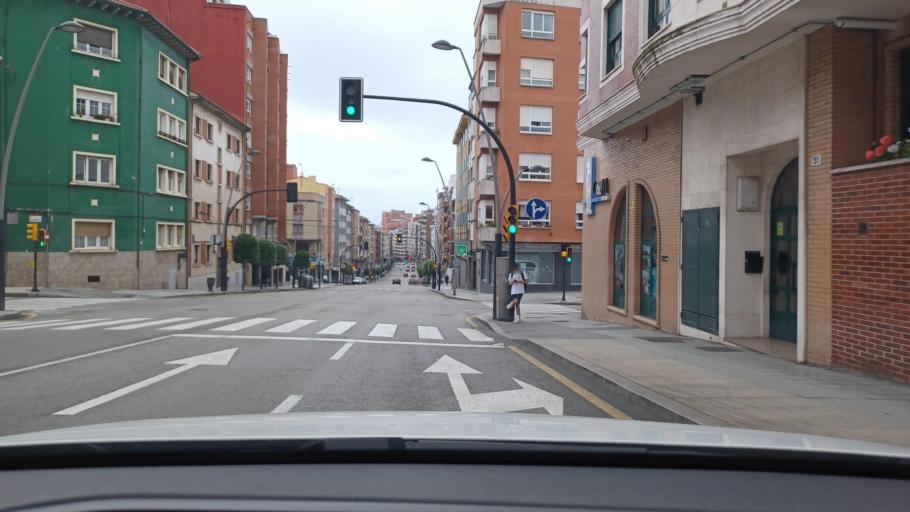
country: ES
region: Asturias
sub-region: Province of Asturias
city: Gijon
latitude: 43.5313
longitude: -5.6545
